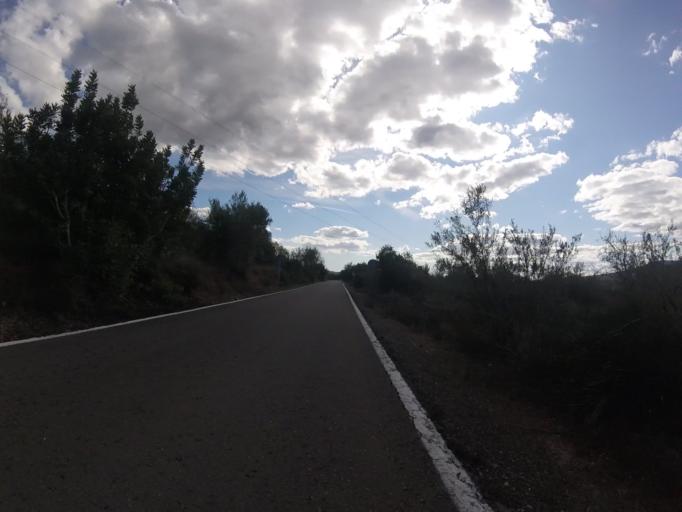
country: ES
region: Valencia
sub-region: Provincia de Castello
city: Cuevas de Vinroma
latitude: 40.3590
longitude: 0.1254
